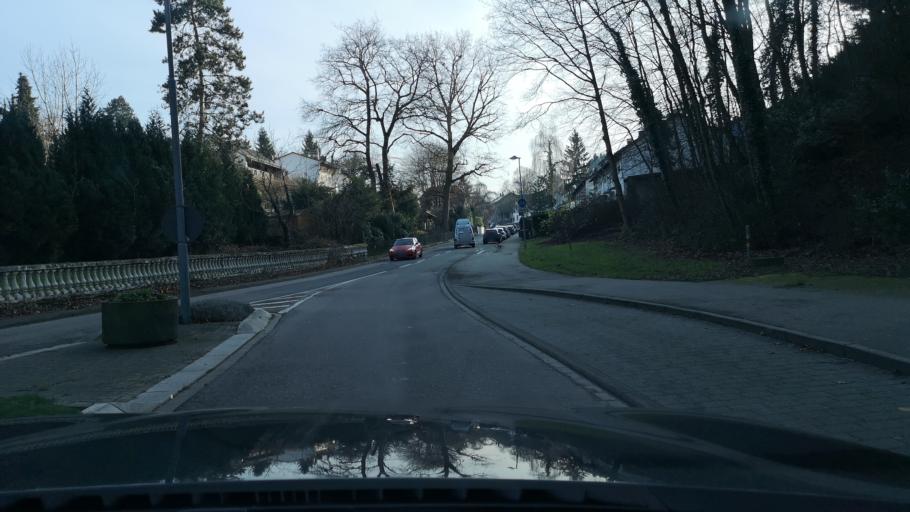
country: DE
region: Baden-Wuerttemberg
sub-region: Karlsruhe Region
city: Ettlingen
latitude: 48.9719
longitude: 8.4755
